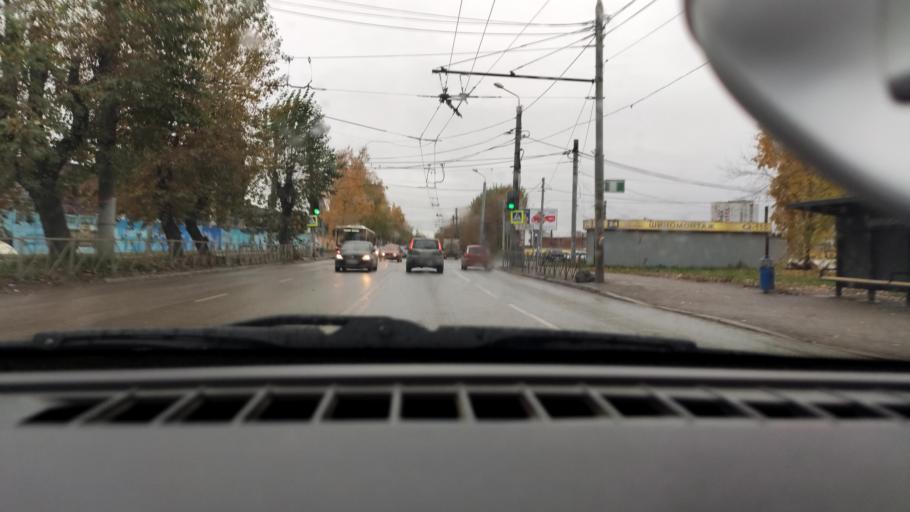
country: RU
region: Perm
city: Perm
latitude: 57.9811
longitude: 56.2468
